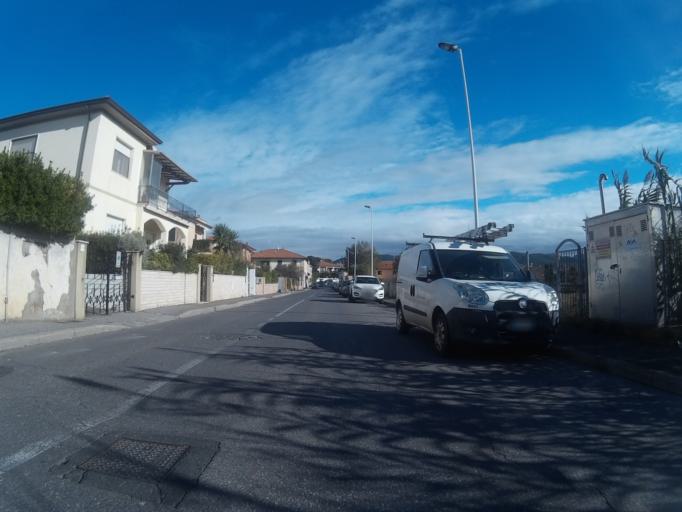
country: IT
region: Tuscany
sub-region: Provincia di Livorno
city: Livorno
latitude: 43.5185
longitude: 10.3357
